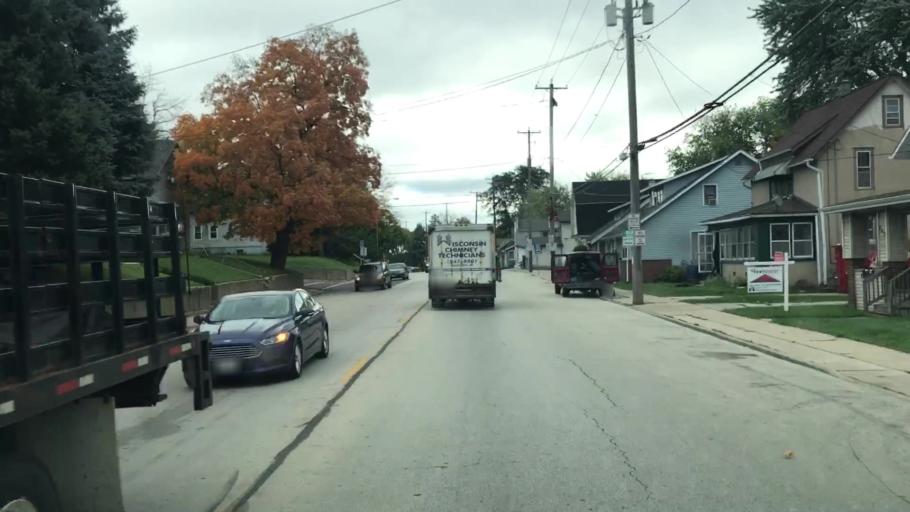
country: US
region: Wisconsin
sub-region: Waukesha County
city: Waukesha
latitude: 43.0077
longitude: -88.2429
